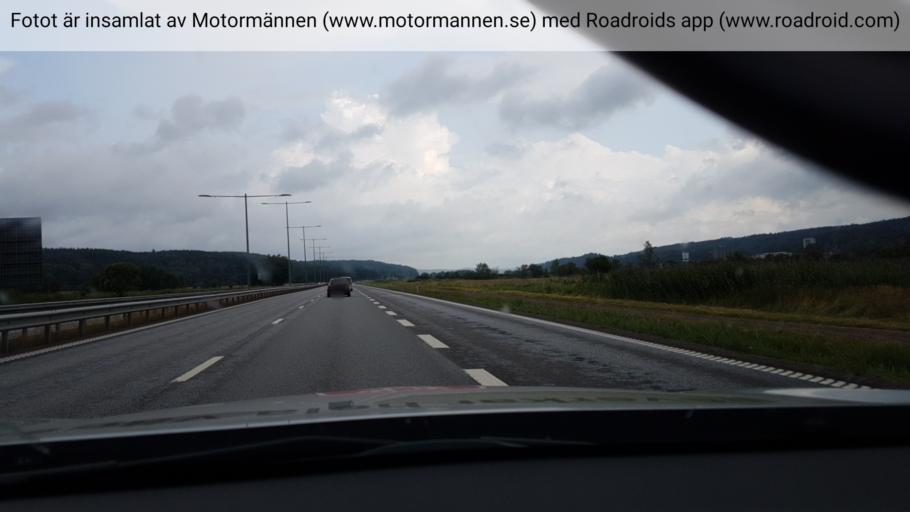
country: SE
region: Vaestra Goetaland
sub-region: Ale Kommun
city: Surte
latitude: 57.8160
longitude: 12.0055
